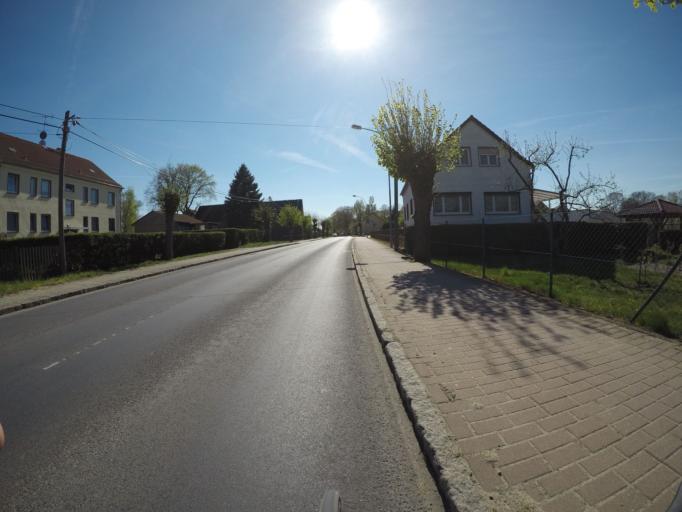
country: DE
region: Brandenburg
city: Rehfelde
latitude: 52.5040
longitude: 13.9268
